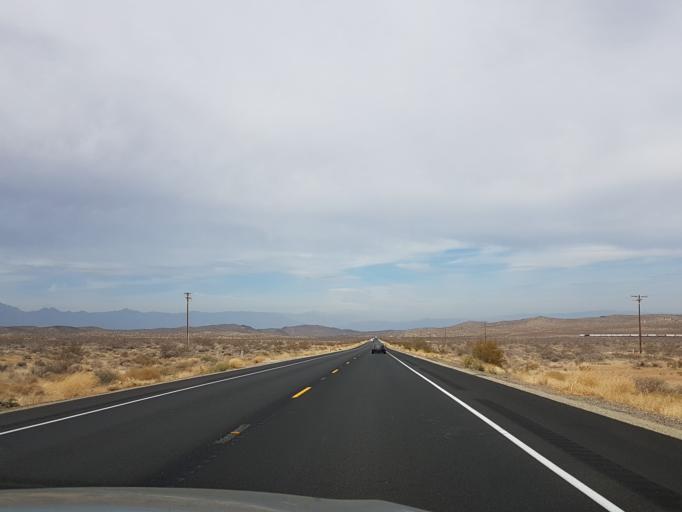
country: US
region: California
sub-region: Kern County
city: Ridgecrest
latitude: 35.5024
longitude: -117.6650
